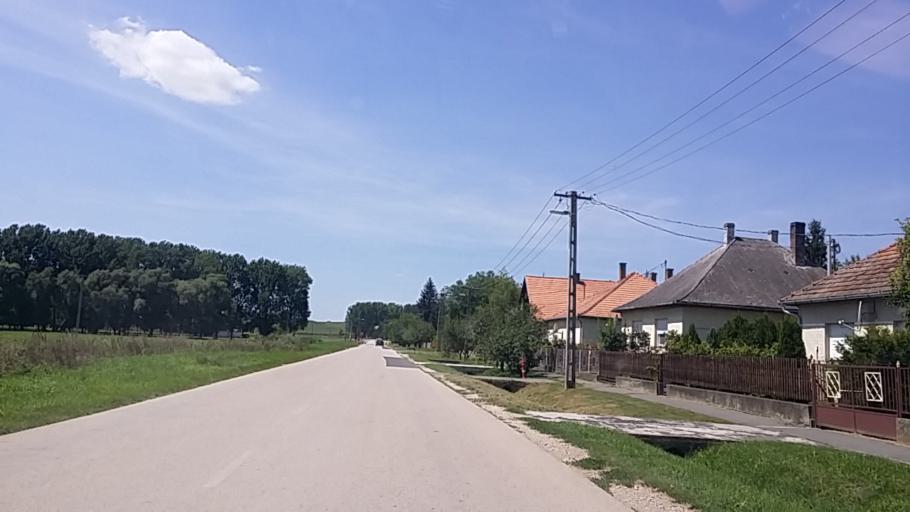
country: HU
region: Somogy
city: Tab
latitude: 46.7472
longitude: 18.1059
